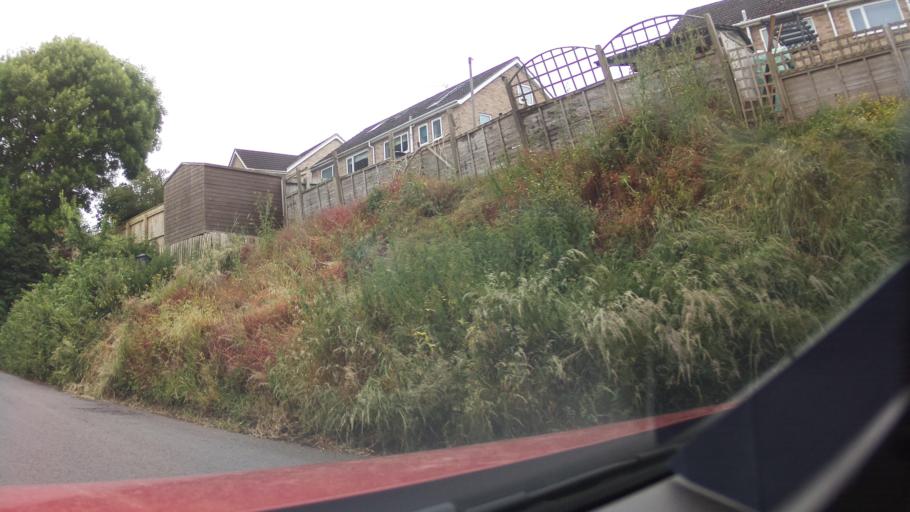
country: GB
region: England
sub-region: Devon
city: Ottery St Mary
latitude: 50.7531
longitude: -3.2687
